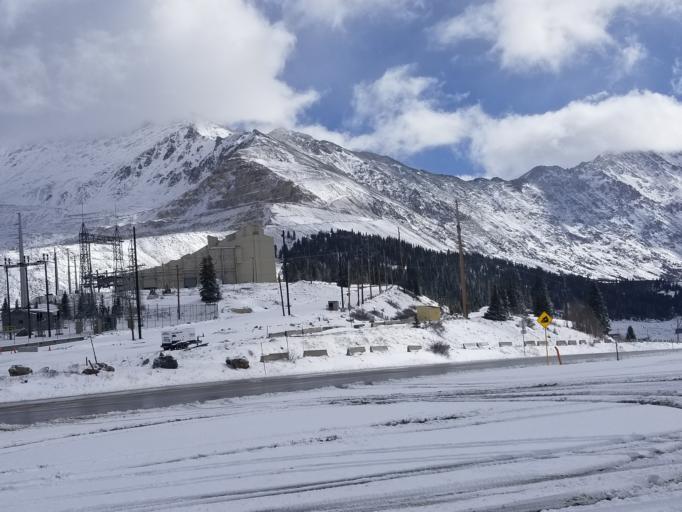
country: US
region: Colorado
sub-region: Lake County
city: Leadville
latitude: 39.3678
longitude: -106.1883
